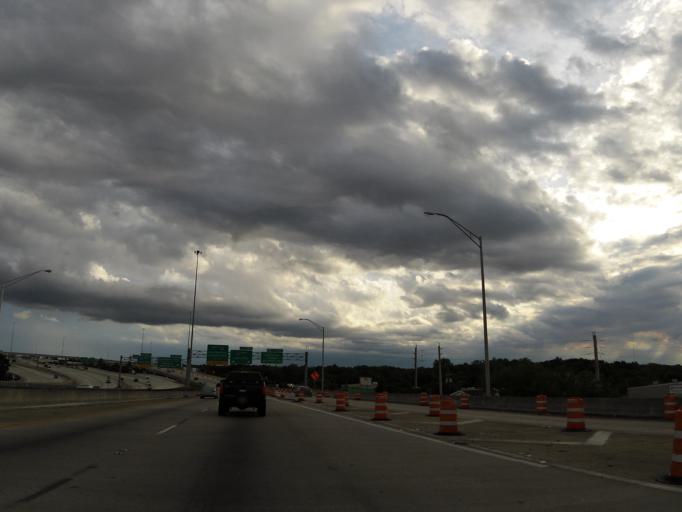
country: US
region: Florida
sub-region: Duval County
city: Jacksonville
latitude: 30.3286
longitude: -81.6776
